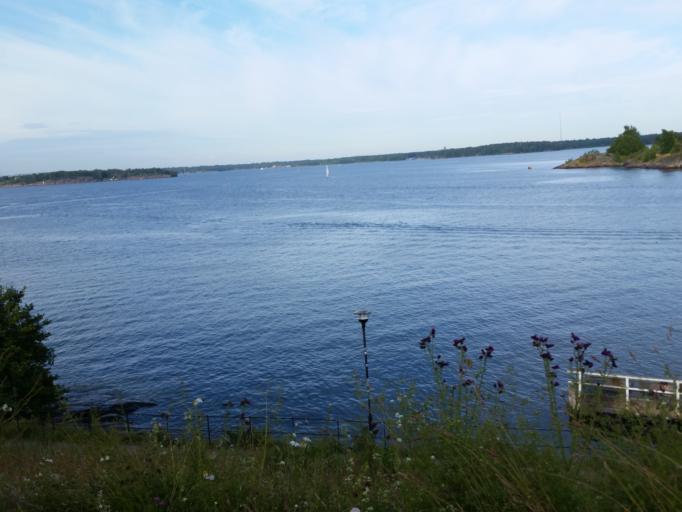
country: FI
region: Uusimaa
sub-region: Helsinki
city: Helsinki
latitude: 60.1401
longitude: 24.9893
